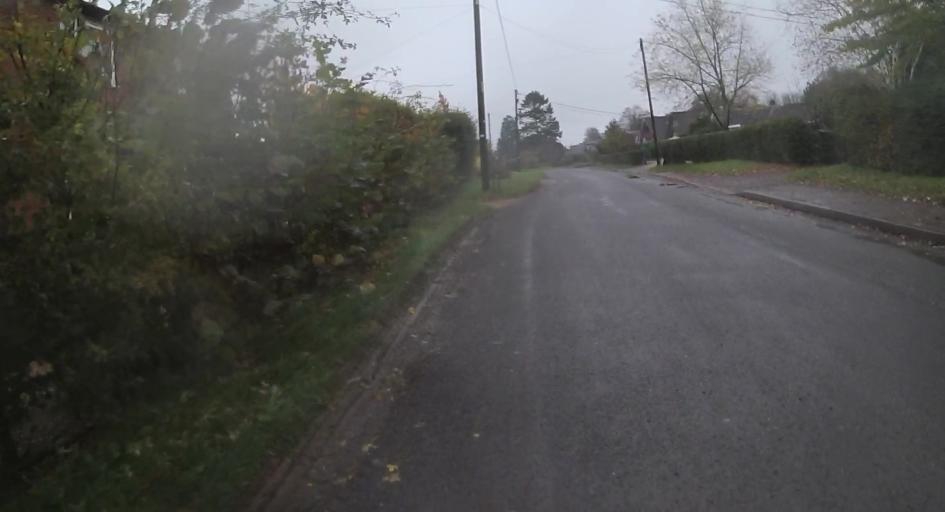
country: GB
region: England
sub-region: Hampshire
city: Four Marks
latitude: 51.1303
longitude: -1.0578
